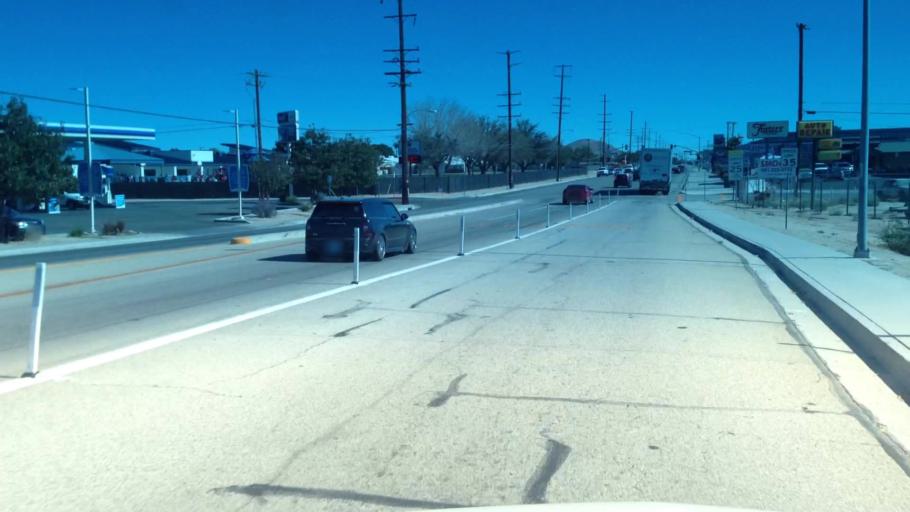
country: US
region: California
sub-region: Kern County
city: Rosamond
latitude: 34.8642
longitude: -118.1700
